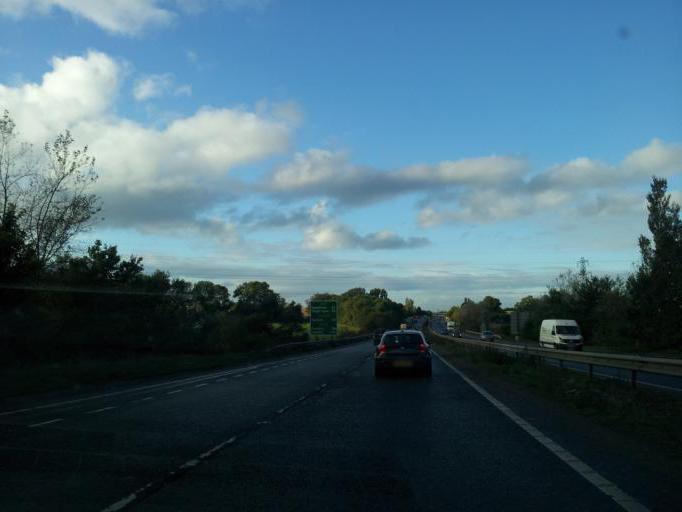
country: GB
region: England
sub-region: Norfolk
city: Thorpe Hamlet
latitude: 52.6046
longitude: 1.3167
